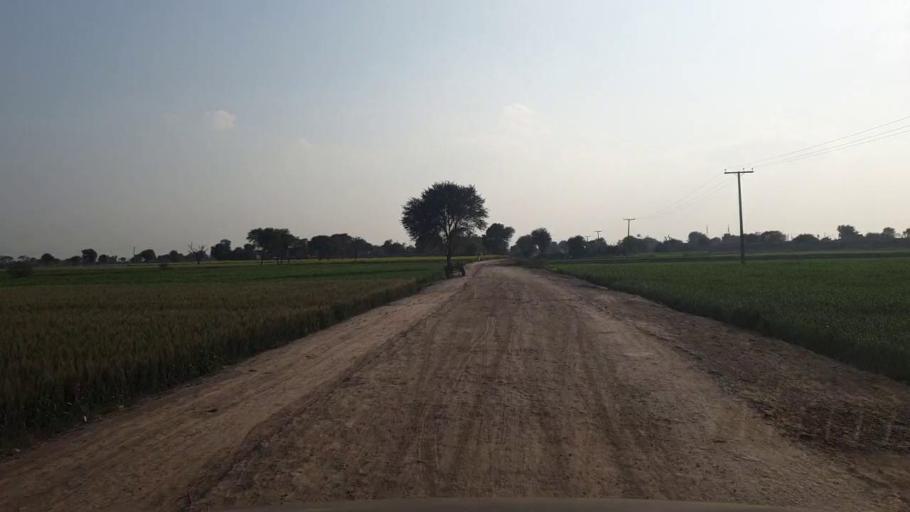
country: PK
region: Sindh
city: Bhit Shah
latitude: 25.7760
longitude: 68.4669
